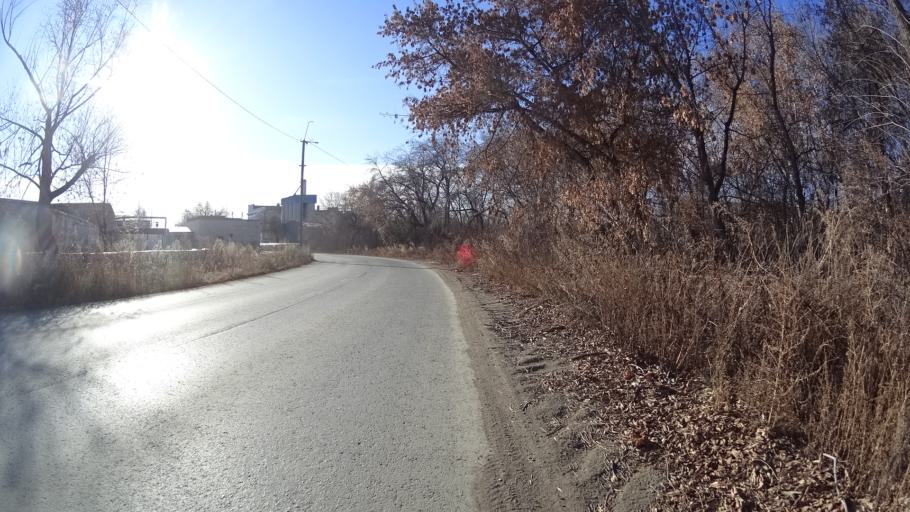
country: RU
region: Chelyabinsk
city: Troitsk
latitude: 54.0431
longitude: 61.6389
